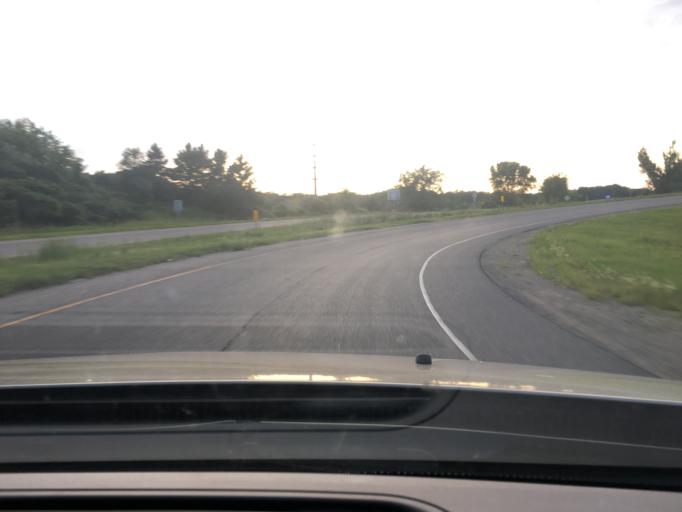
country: US
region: Minnesota
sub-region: Dakota County
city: West Saint Paul
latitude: 44.8765
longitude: -93.0820
